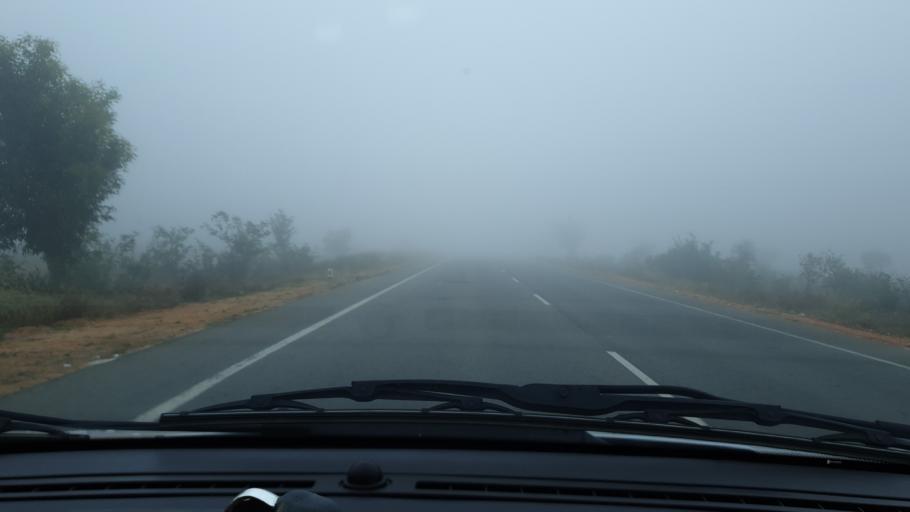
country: IN
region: Telangana
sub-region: Mahbubnagar
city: Nagar Karnul
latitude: 16.6765
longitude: 78.5290
